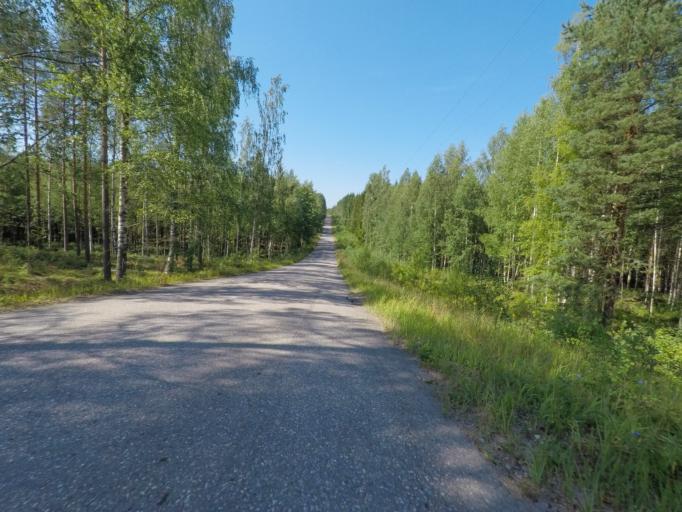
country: FI
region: Southern Savonia
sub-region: Mikkeli
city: Puumala
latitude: 61.4224
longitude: 28.1396
